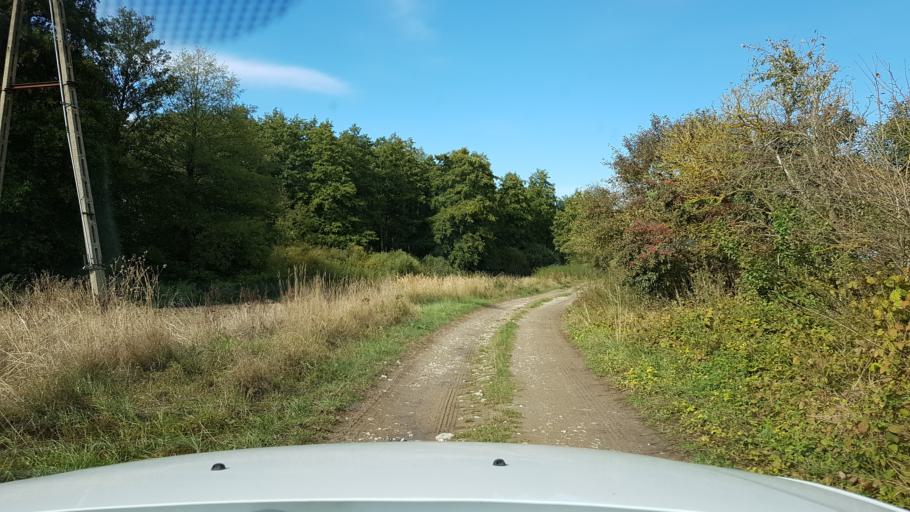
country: PL
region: West Pomeranian Voivodeship
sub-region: Powiat gryfinski
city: Banie
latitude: 53.1211
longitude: 14.6496
